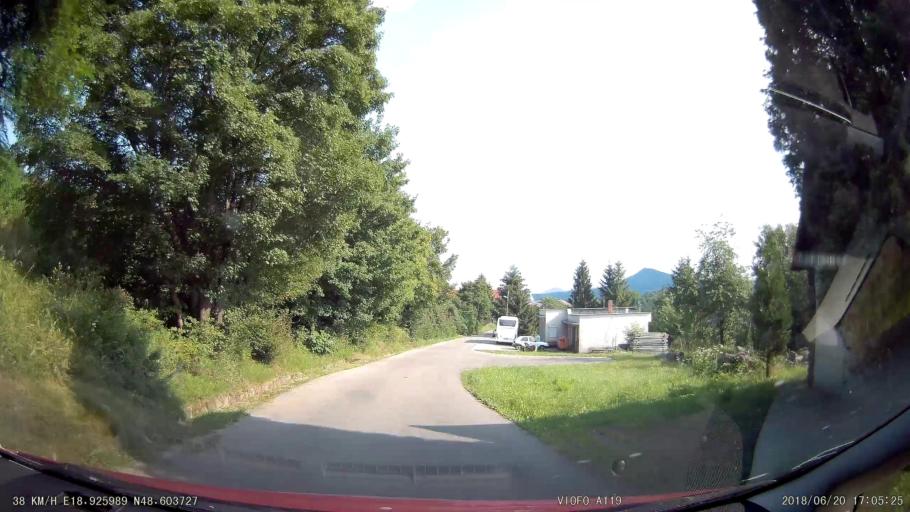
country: SK
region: Banskobystricky
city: Ziar nad Hronom
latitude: 48.6037
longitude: 18.9260
